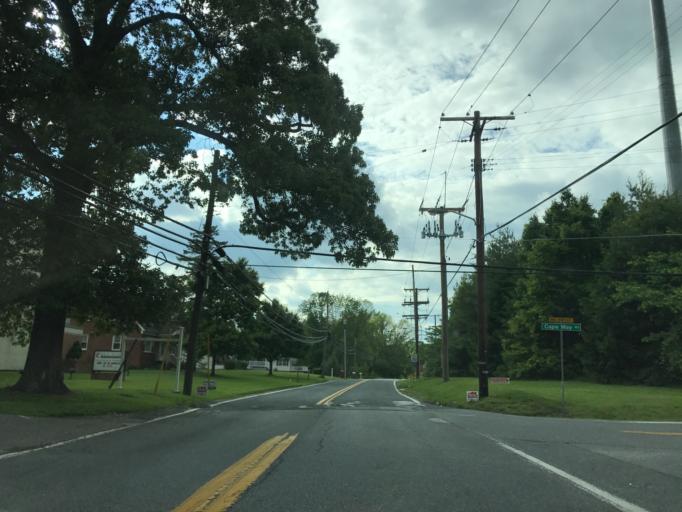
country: US
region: Maryland
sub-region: Baltimore County
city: Middle River
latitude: 39.2949
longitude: -76.4314
